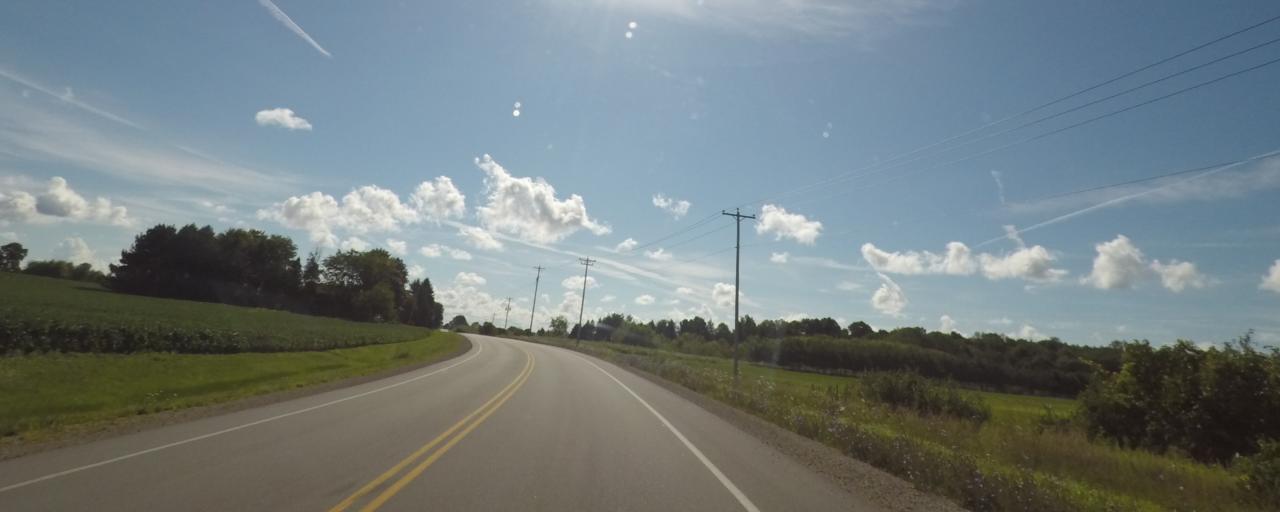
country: US
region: Wisconsin
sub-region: Jefferson County
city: Ixonia
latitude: 43.0679
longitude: -88.6294
